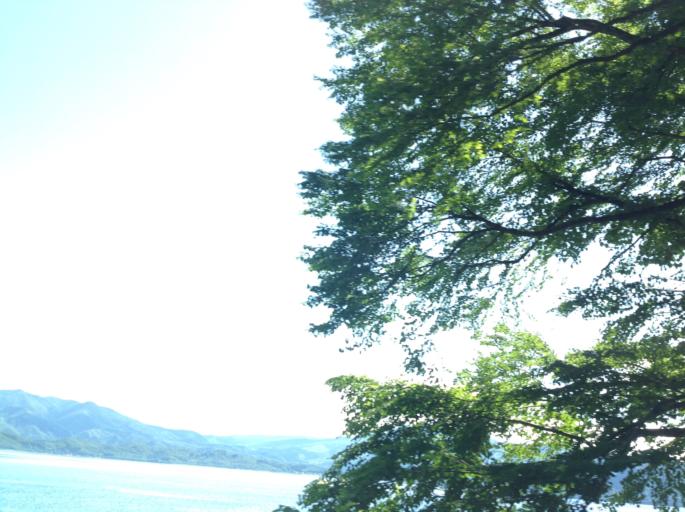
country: JP
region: Akita
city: Kakunodatemachi
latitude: 39.7099
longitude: 140.6369
